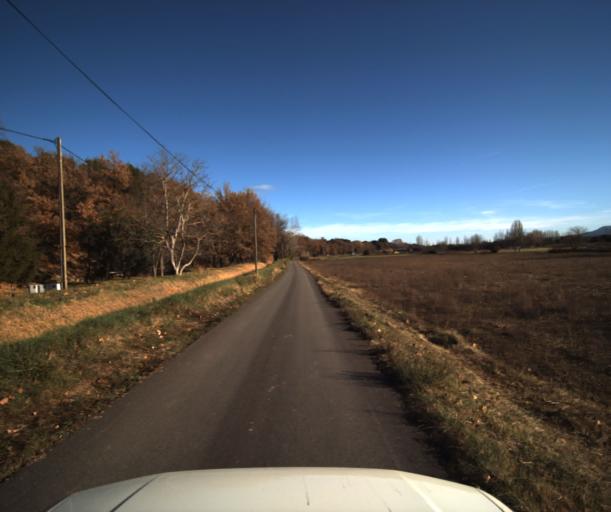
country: FR
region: Provence-Alpes-Cote d'Azur
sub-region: Departement du Vaucluse
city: Pertuis
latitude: 43.6971
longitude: 5.4701
